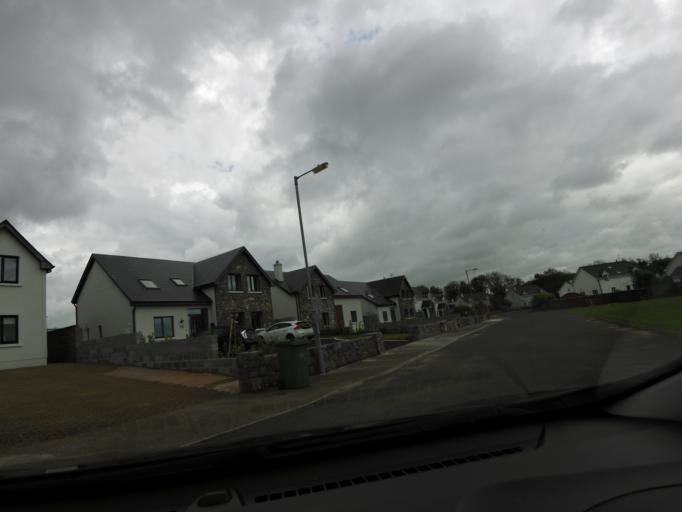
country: IE
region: Connaught
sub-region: County Galway
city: Athenry
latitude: 53.2768
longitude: -8.6415
